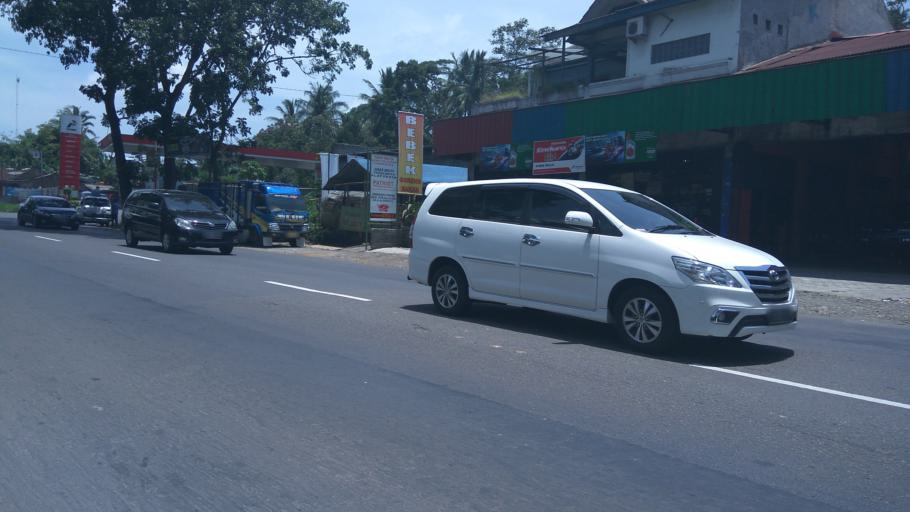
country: ID
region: Central Java
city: Salatiga
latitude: -7.4328
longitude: 110.5313
